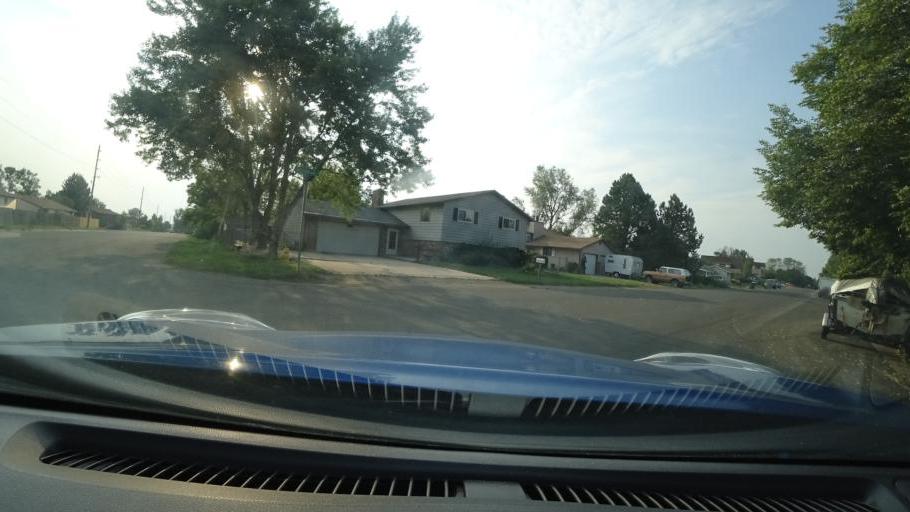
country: US
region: Colorado
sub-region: Adams County
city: Aurora
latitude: 39.7438
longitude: -104.7676
